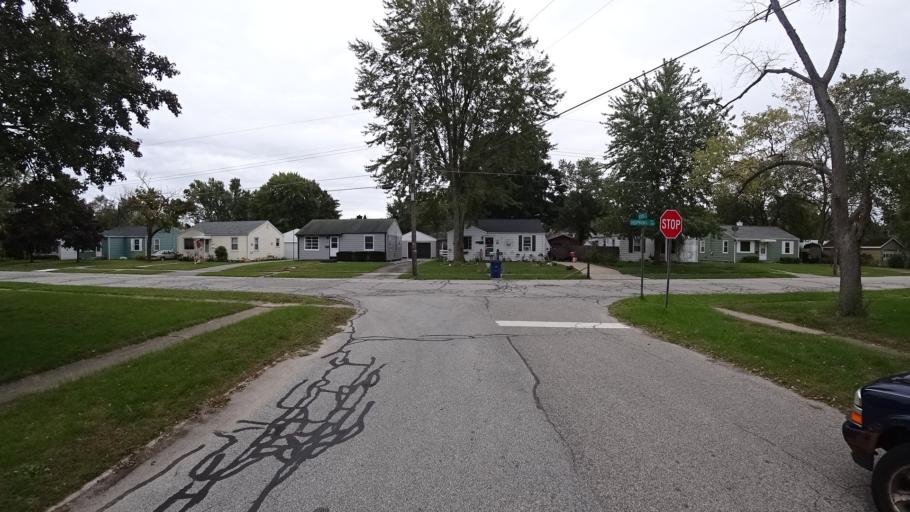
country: US
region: Indiana
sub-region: LaPorte County
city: Michigan City
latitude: 41.6958
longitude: -86.8981
